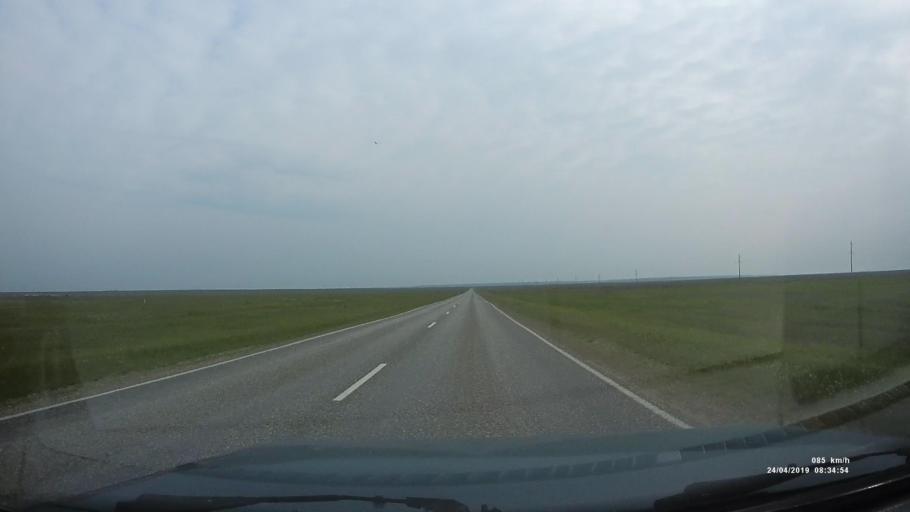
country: RU
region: Kalmykiya
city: Arshan'
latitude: 46.1936
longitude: 43.9112
